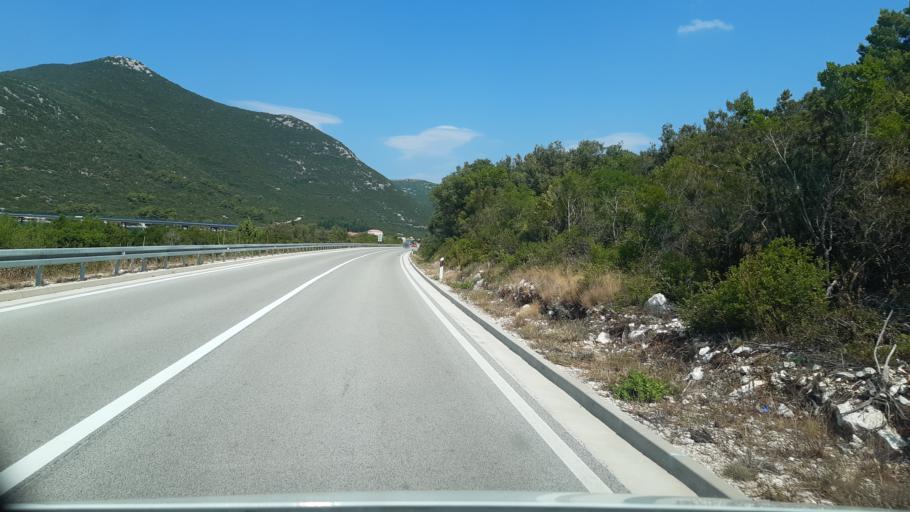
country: HR
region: Dubrovacko-Neretvanska
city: Ston
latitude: 42.8634
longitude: 17.7030
